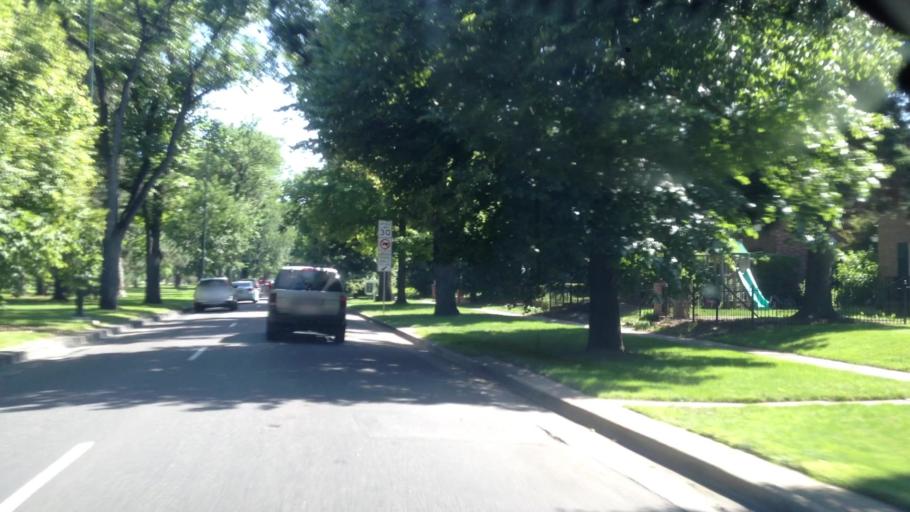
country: US
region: Colorado
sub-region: Arapahoe County
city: Glendale
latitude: 39.7431
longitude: -104.9128
